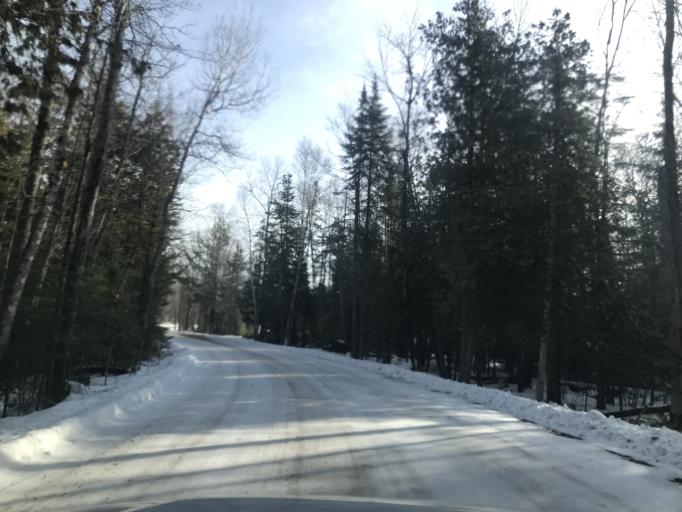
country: US
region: Wisconsin
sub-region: Door County
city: Sturgeon Bay
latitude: 45.1536
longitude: -87.0574
